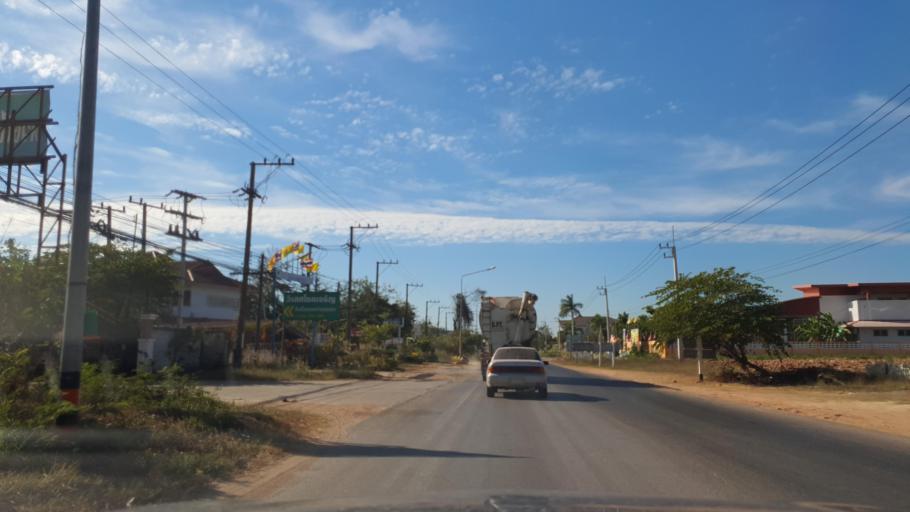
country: TH
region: Kalasin
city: Kuchinarai
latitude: 16.5340
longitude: 104.0729
